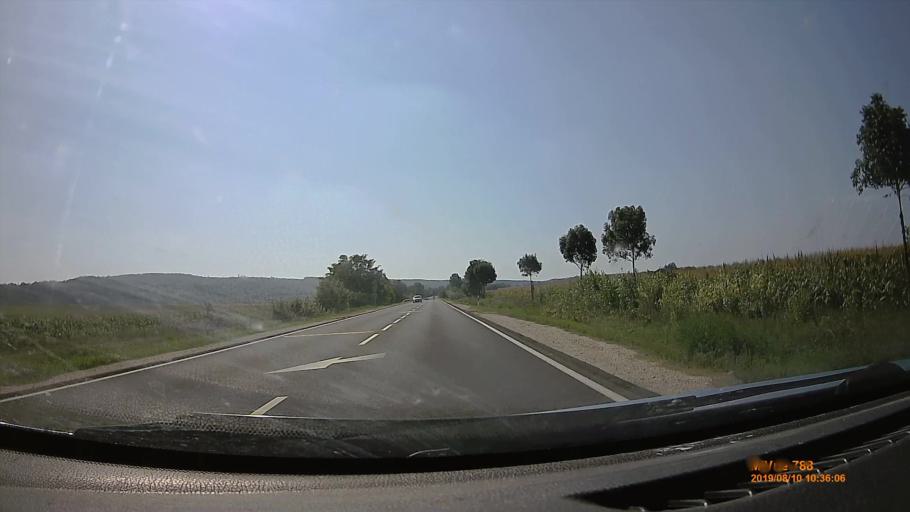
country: HU
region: Somogy
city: Balatonszarszo
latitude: 46.8320
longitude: 17.8484
